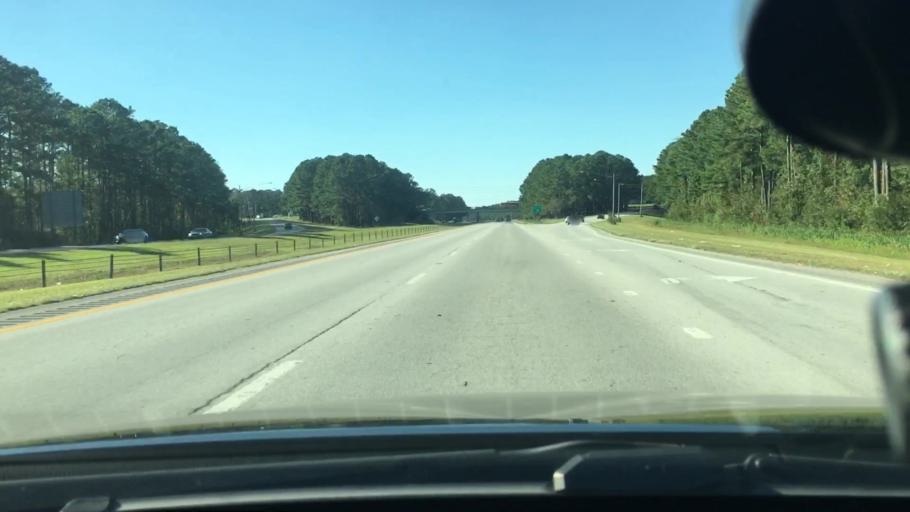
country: US
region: North Carolina
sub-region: Craven County
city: Trent Woods
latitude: 35.1100
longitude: -77.0932
